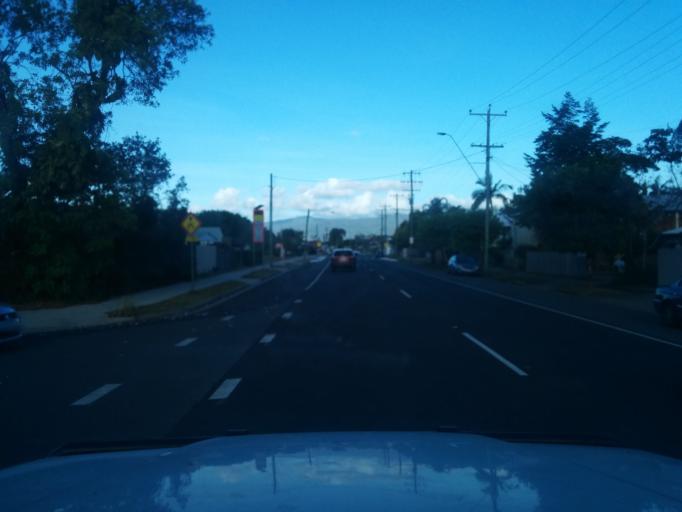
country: AU
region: Queensland
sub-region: Cairns
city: Woree
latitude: -16.9434
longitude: 145.7363
